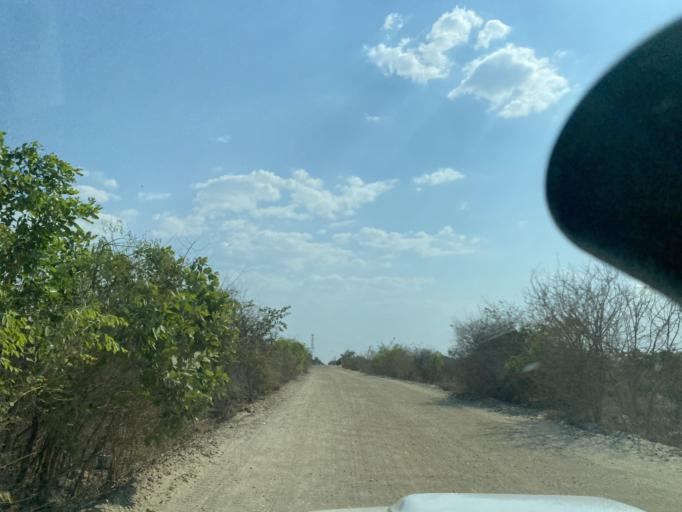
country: ZM
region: Lusaka
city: Lusaka
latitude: -15.3646
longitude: 28.0882
